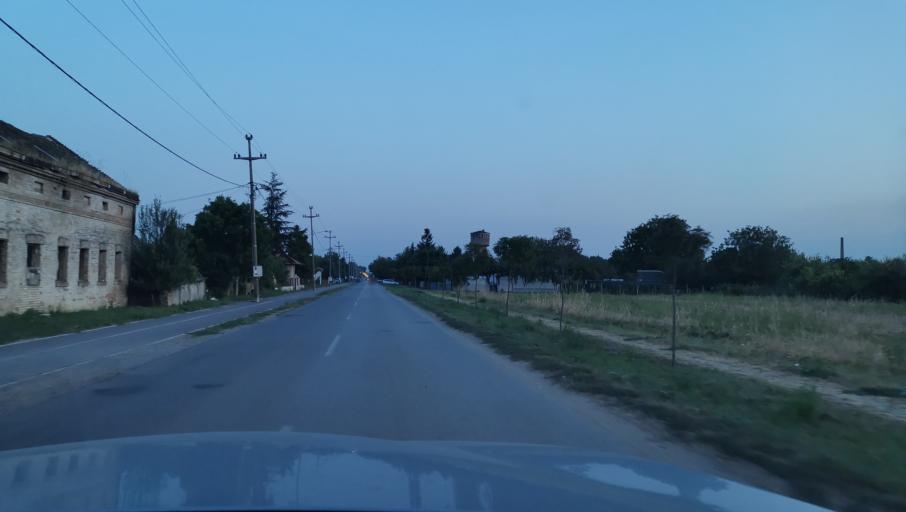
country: RS
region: Central Serbia
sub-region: Belgrade
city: Obrenovac
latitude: 44.6822
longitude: 20.2022
